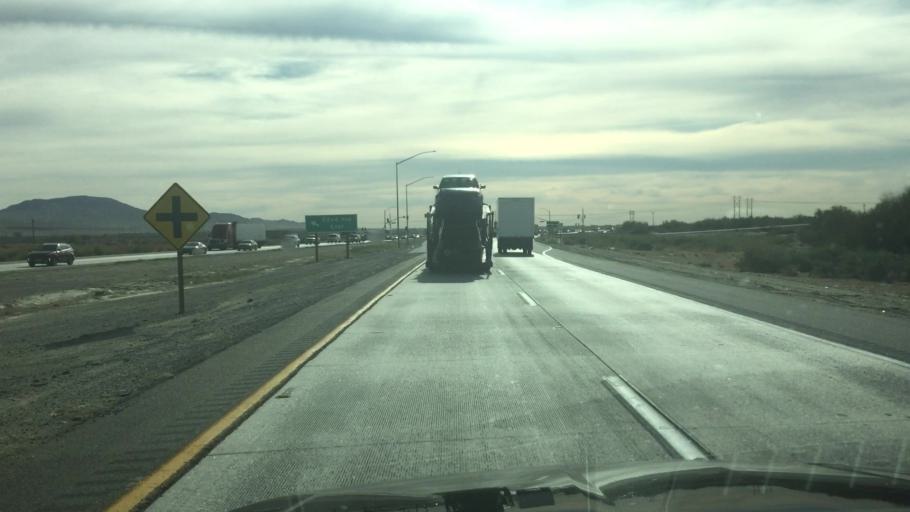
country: US
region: California
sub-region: Riverside County
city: Coachella
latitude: 33.6760
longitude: -116.1501
